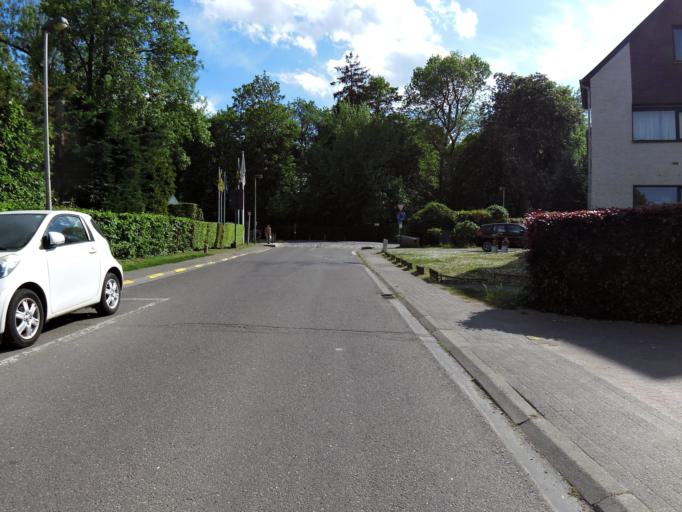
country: BE
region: Flanders
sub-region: Provincie Vlaams-Brabant
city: Wezembeek-Oppem
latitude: 50.8447
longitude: 4.4902
